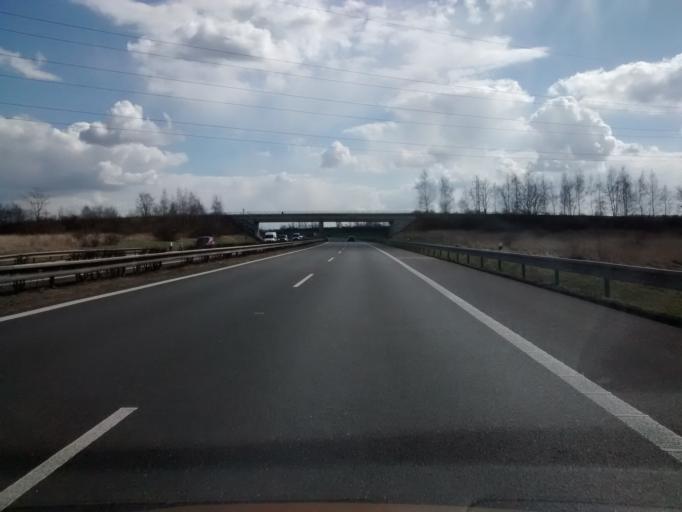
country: CZ
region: Central Bohemia
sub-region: Okres Melnik
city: Veltrusy
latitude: 50.2798
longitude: 14.3535
